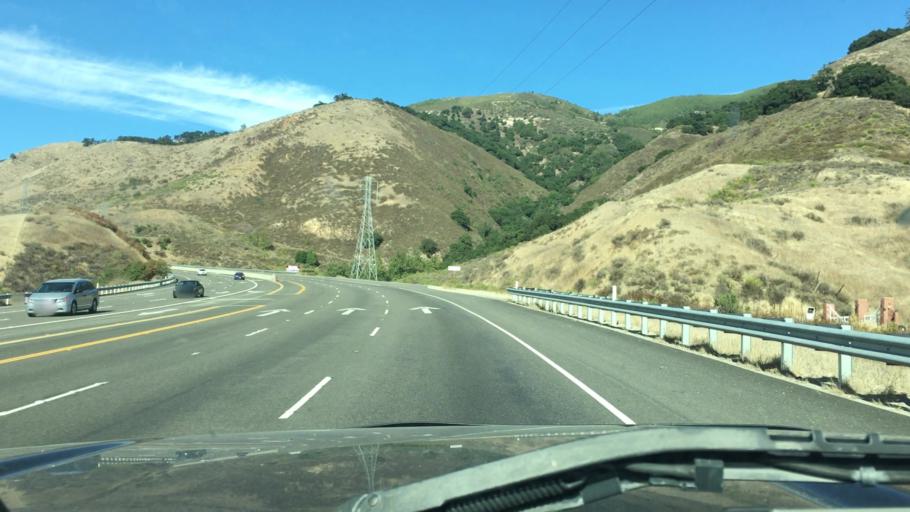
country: US
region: California
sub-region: San Luis Obispo County
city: San Luis Obispo
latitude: 35.3250
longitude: -120.6203
